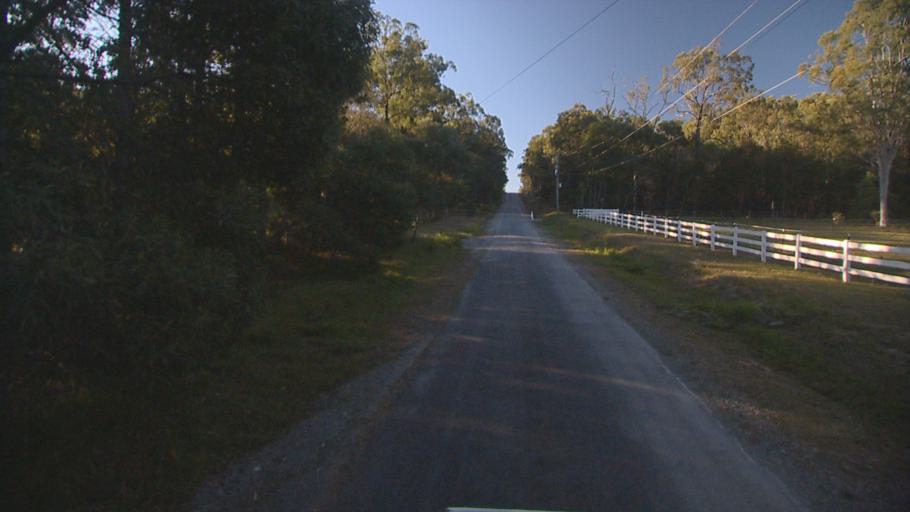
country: AU
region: Queensland
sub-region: Logan
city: Chambers Flat
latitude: -27.7687
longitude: 153.1325
